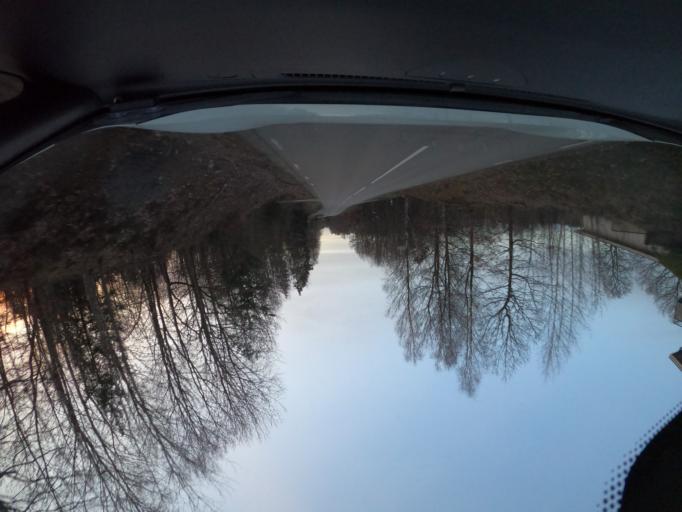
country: SE
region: Vaestra Goetaland
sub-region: Harryda Kommun
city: Landvetter
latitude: 57.6362
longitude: 12.1815
